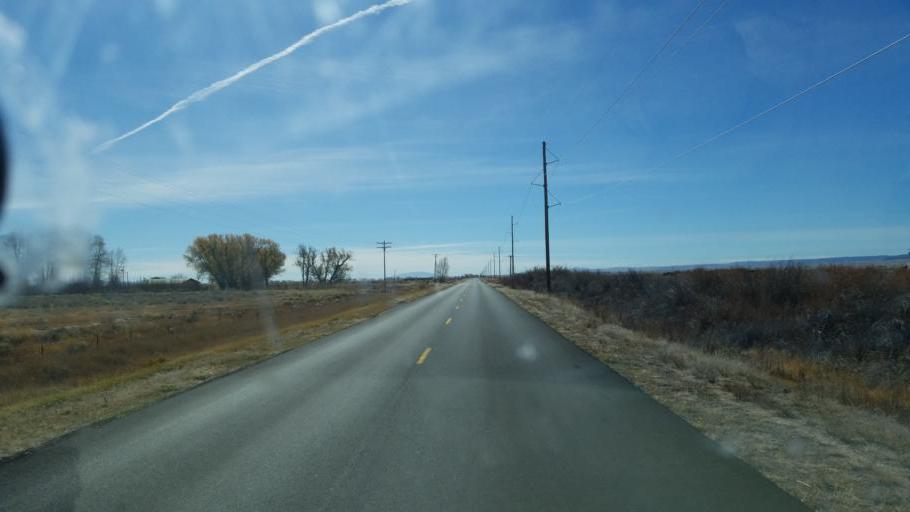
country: US
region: Colorado
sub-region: Rio Grande County
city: Monte Vista
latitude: 37.5263
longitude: -106.0943
